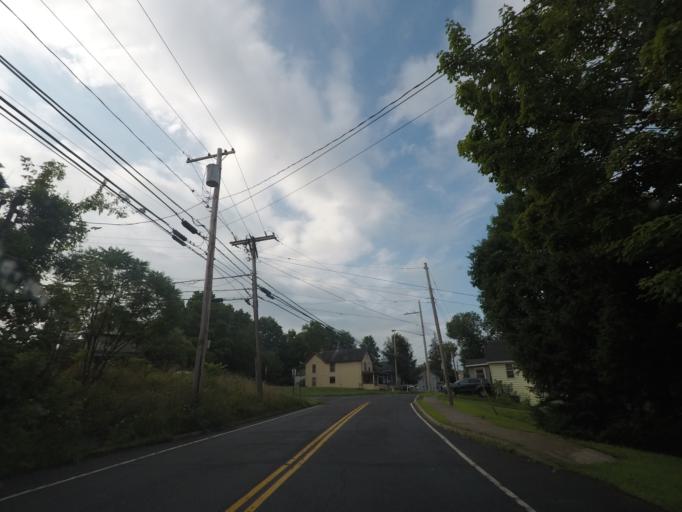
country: US
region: New York
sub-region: Rensselaer County
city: Nassau
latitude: 42.5208
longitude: -73.6081
